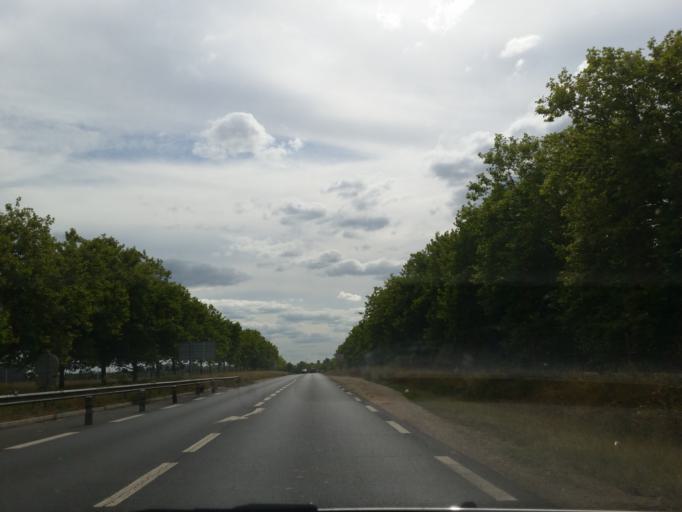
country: FR
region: Centre
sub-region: Departement du Loir-et-Cher
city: La Chaussee-Saint-Victor
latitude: 47.6155
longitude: 1.3450
